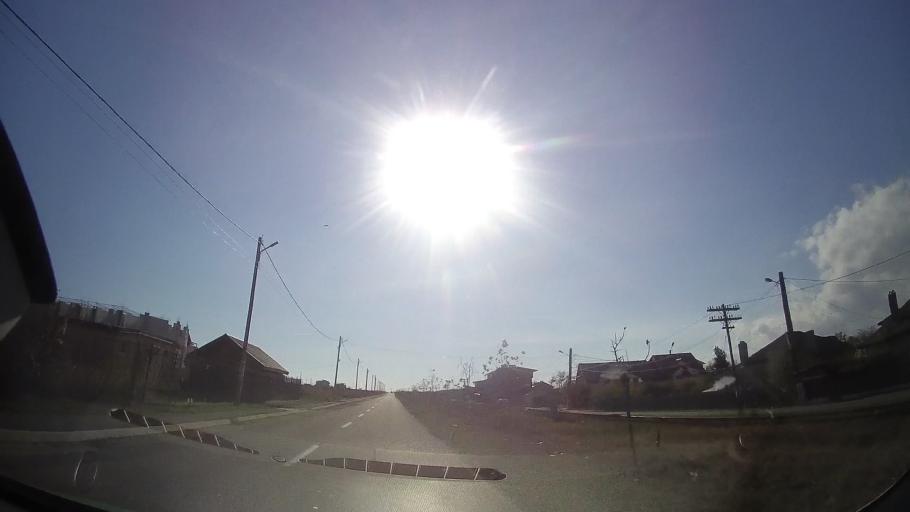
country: RO
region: Constanta
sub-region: Comuna Costinesti
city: Schitu
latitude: 43.9398
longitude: 28.6317
